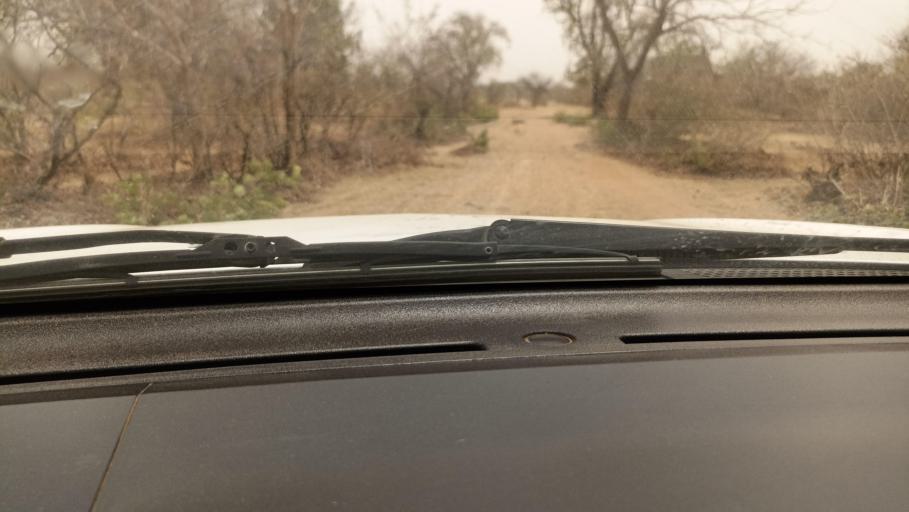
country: BF
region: Boucle du Mouhoun
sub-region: Province du Nayala
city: Toma
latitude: 12.8693
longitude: -2.7527
